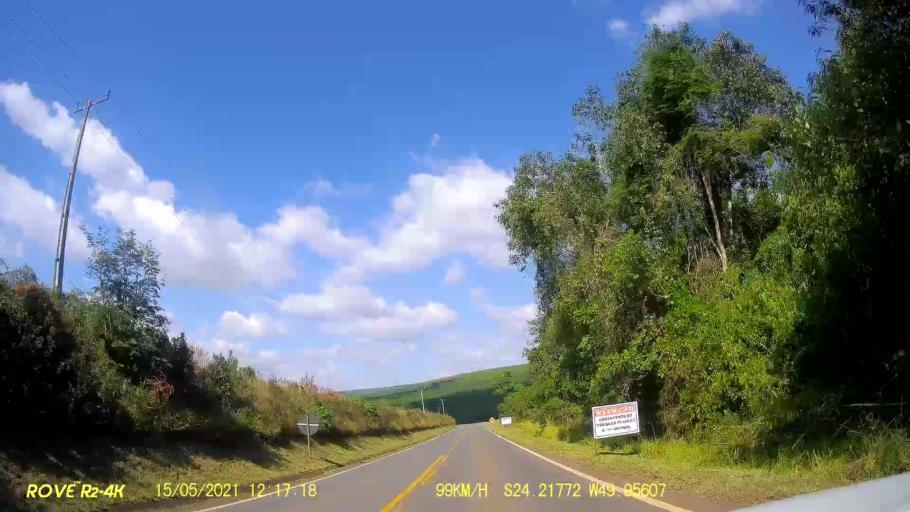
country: BR
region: Parana
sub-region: Jaguariaiva
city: Jaguariaiva
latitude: -24.2177
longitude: -49.9561
